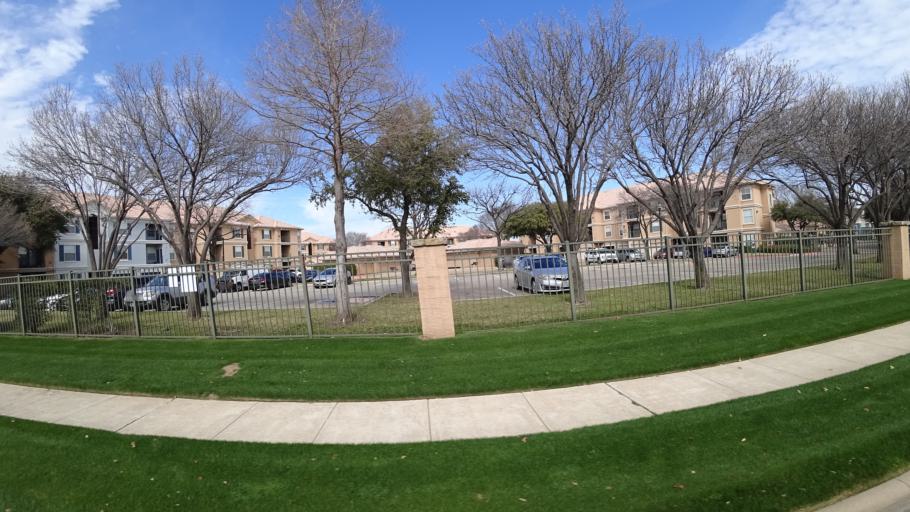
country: US
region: Texas
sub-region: Denton County
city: Lewisville
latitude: 33.0084
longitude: -96.9654
